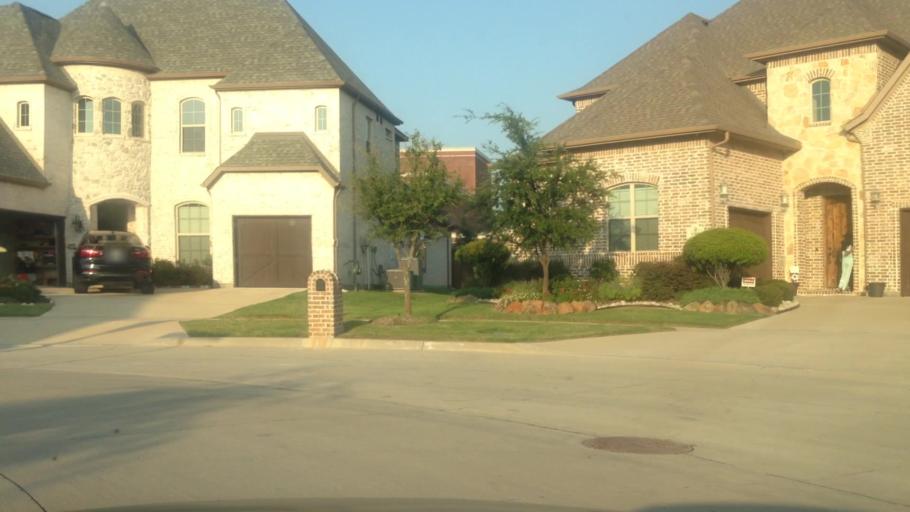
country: US
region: Texas
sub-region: Denton County
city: The Colony
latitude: 33.1308
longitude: -96.8666
